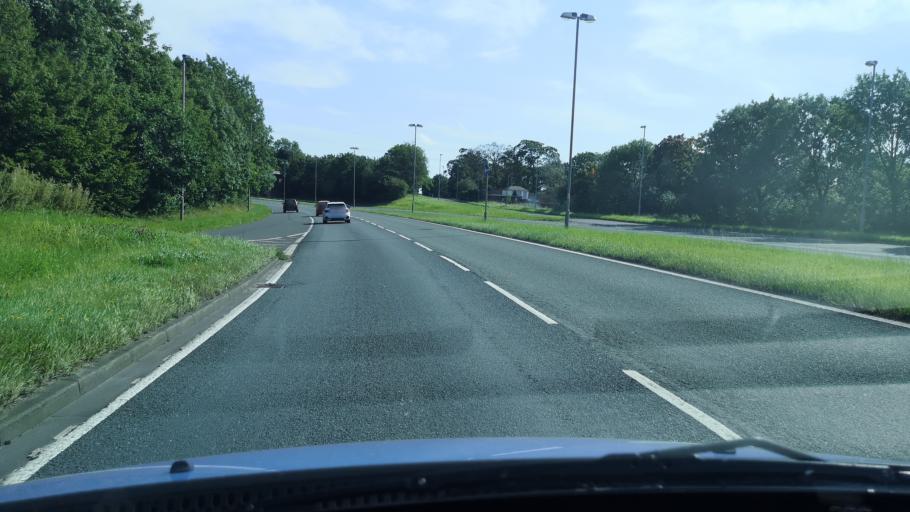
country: GB
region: England
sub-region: City and Borough of Leeds
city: Lofthouse
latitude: 53.7110
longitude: -1.5302
